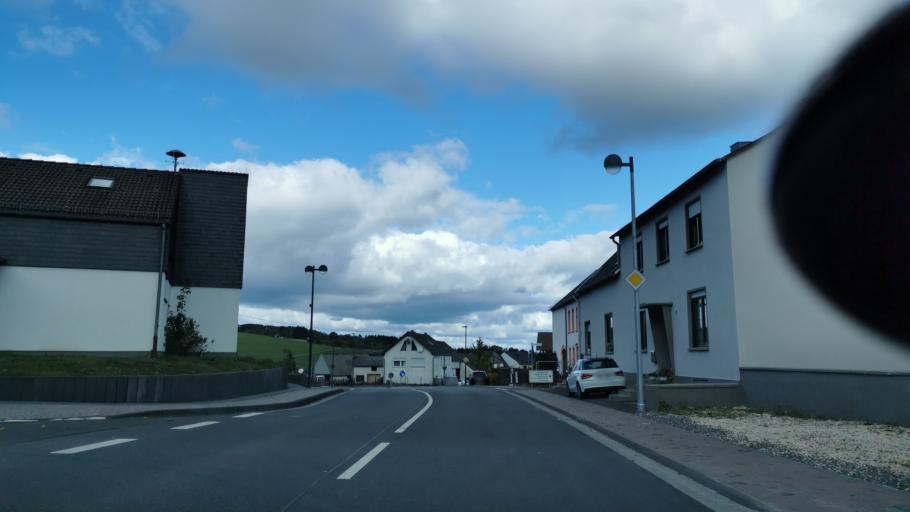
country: DE
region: Rheinland-Pfalz
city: Dockweiler
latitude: 50.2500
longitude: 6.7798
